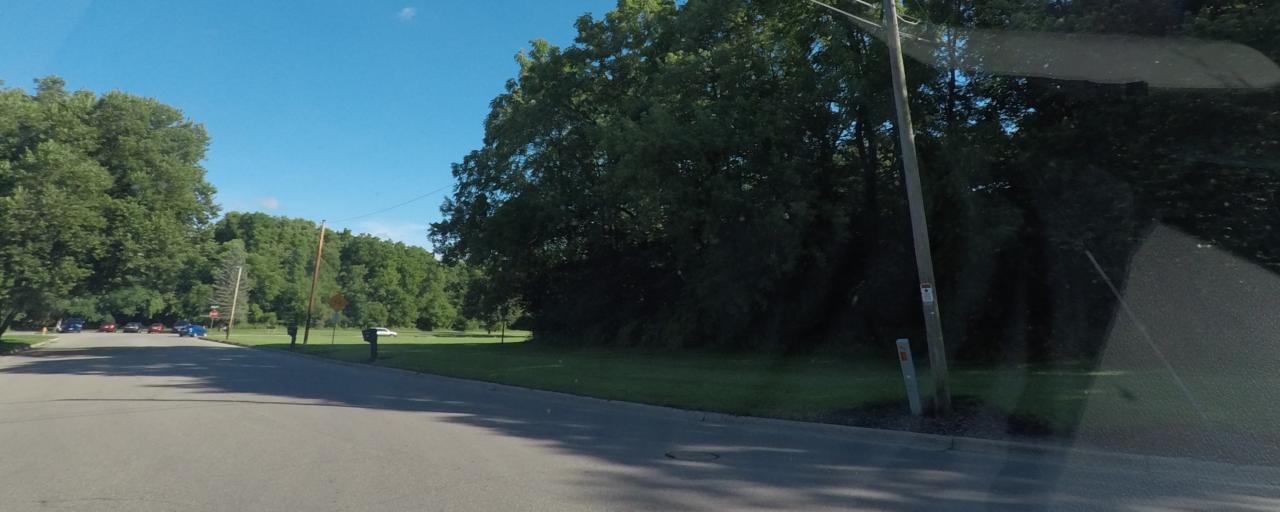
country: US
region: Wisconsin
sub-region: Rock County
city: Janesville
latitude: 42.6824
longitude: -88.9890
